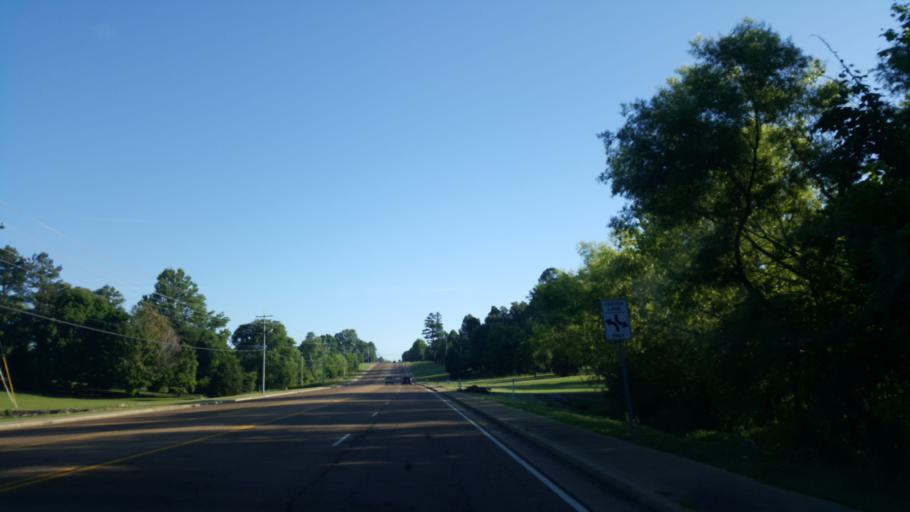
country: US
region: Tennessee
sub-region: Henderson County
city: Lexington
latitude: 35.6693
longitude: -88.3843
